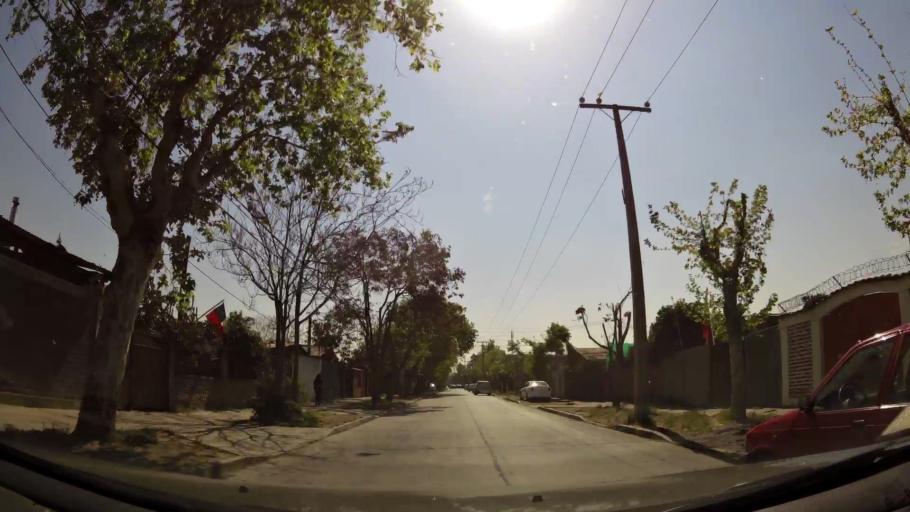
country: CL
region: Santiago Metropolitan
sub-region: Provincia de Maipo
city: San Bernardo
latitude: -33.5971
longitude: -70.7100
